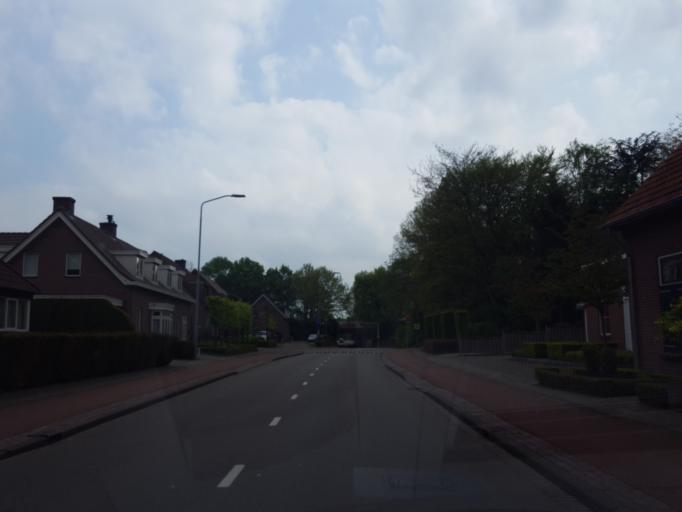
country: NL
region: North Brabant
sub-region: Gemeente Veldhoven
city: Veldhoven
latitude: 51.3993
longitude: 5.3983
